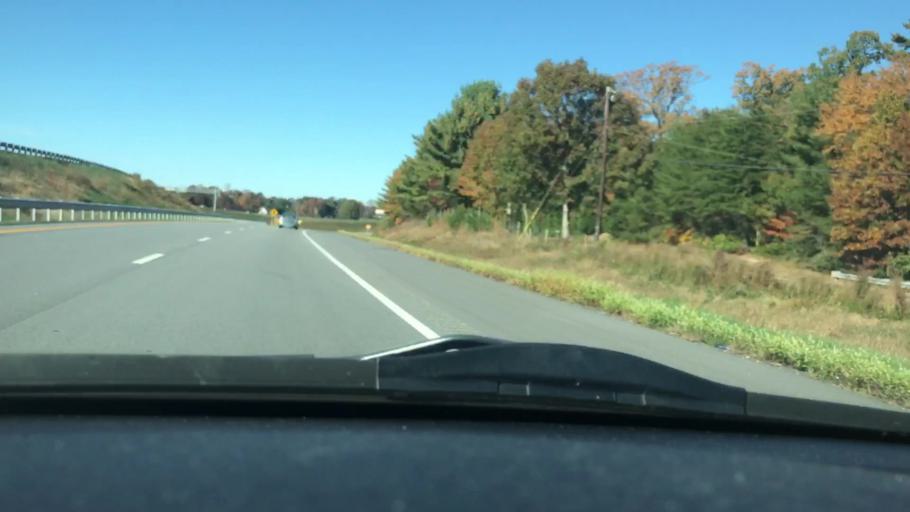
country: US
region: North Carolina
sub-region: Guilford County
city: Stokesdale
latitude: 36.2825
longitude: -79.9387
